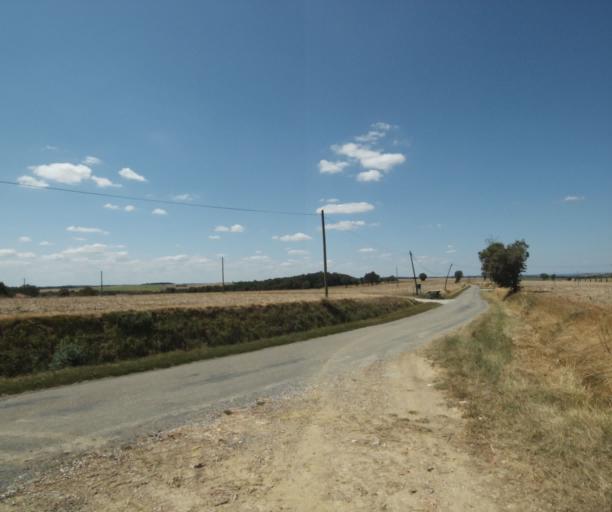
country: FR
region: Midi-Pyrenees
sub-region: Departement de la Haute-Garonne
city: Saint-Felix-Lauragais
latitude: 43.4859
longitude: 1.8615
